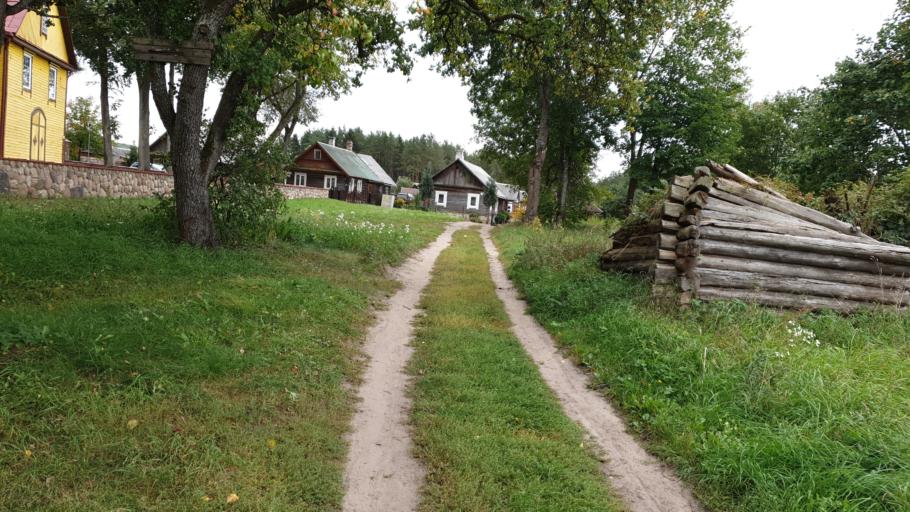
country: LT
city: Grigiskes
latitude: 54.7315
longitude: 25.0432
